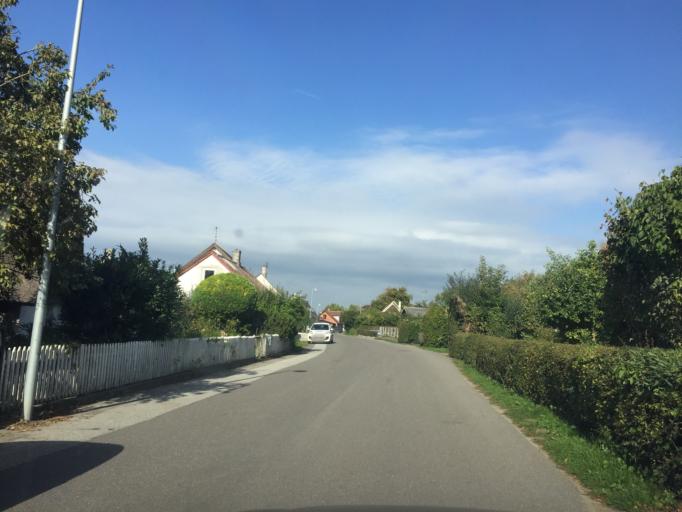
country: DK
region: Zealand
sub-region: Guldborgsund Kommune
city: Stubbekobing
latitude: 54.9221
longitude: 12.0477
